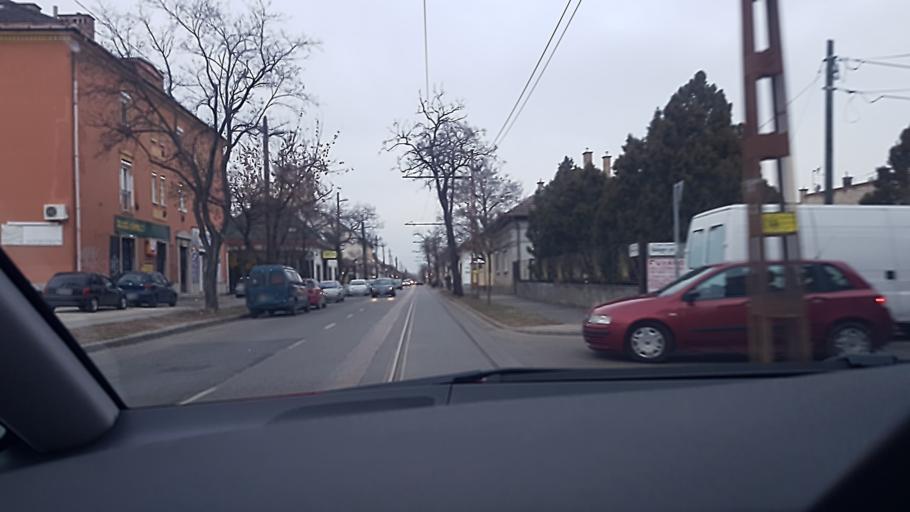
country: HU
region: Budapest
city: Budapest XX. keruelet
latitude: 47.4417
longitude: 19.1147
